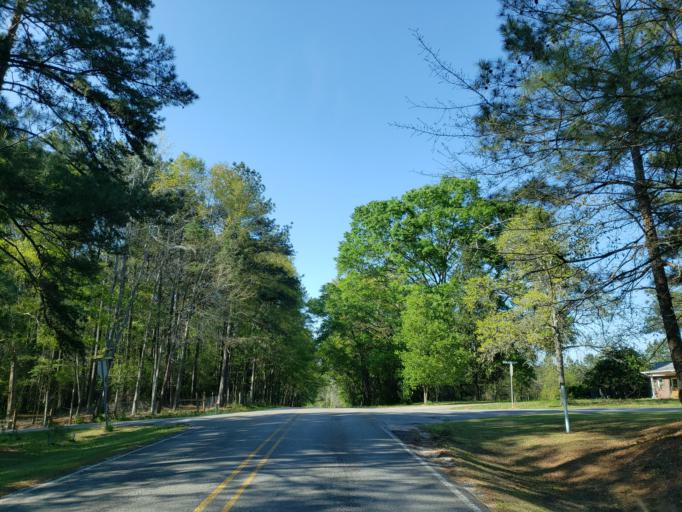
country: US
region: Mississippi
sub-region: Forrest County
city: Rawls Springs
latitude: 31.5285
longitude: -89.3594
